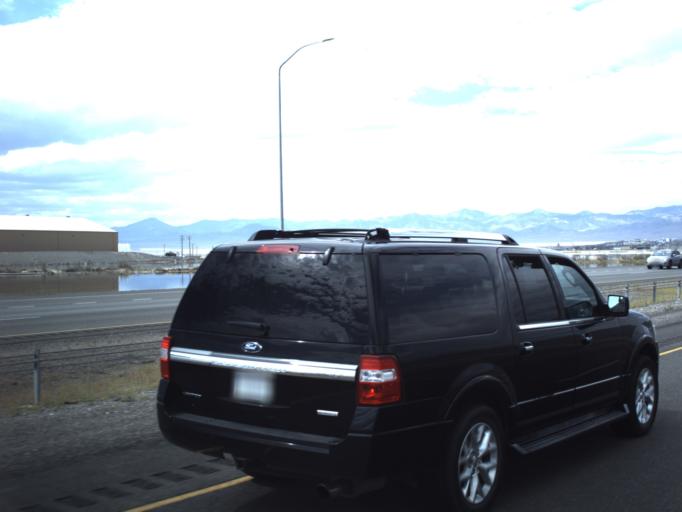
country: US
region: Utah
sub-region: Tooele County
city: Wendover
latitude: 40.7430
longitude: -113.9766
